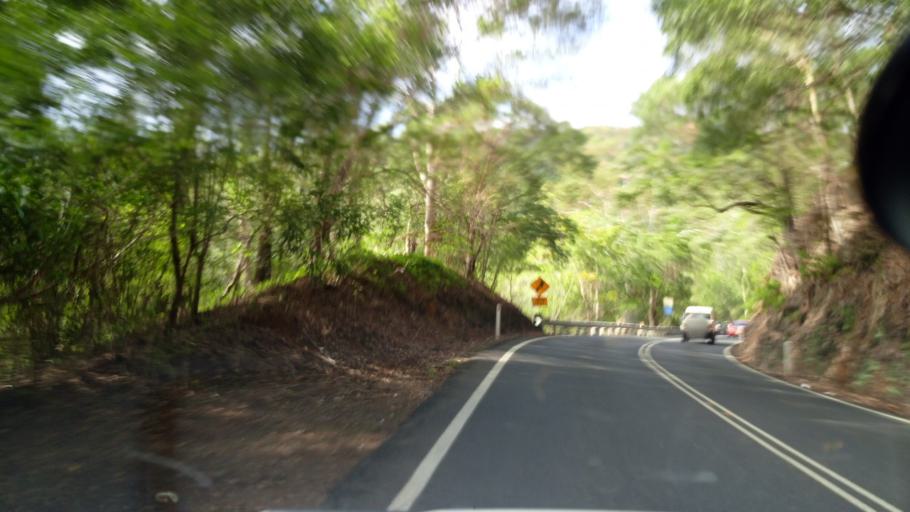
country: AU
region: Queensland
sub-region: Cairns
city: Redlynch
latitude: -16.8410
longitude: 145.6822
